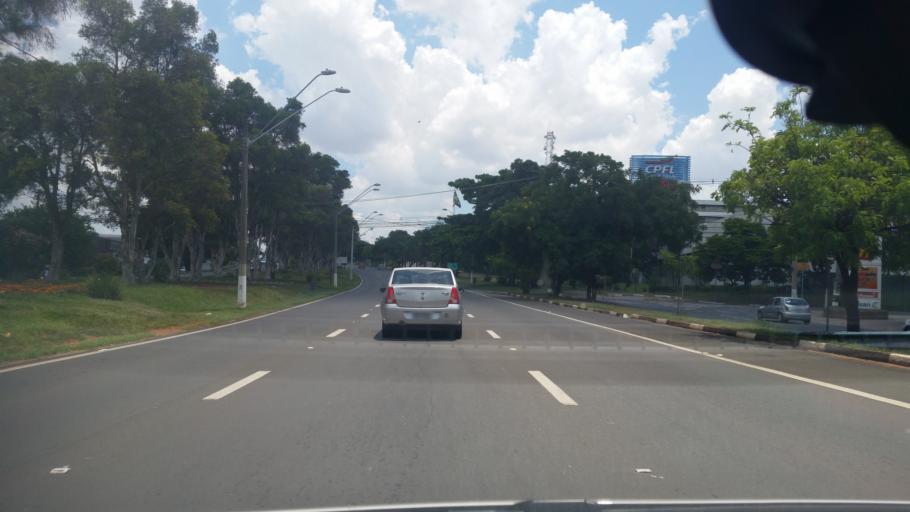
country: BR
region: Sao Paulo
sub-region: Campinas
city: Campinas
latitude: -22.8558
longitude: -47.0444
